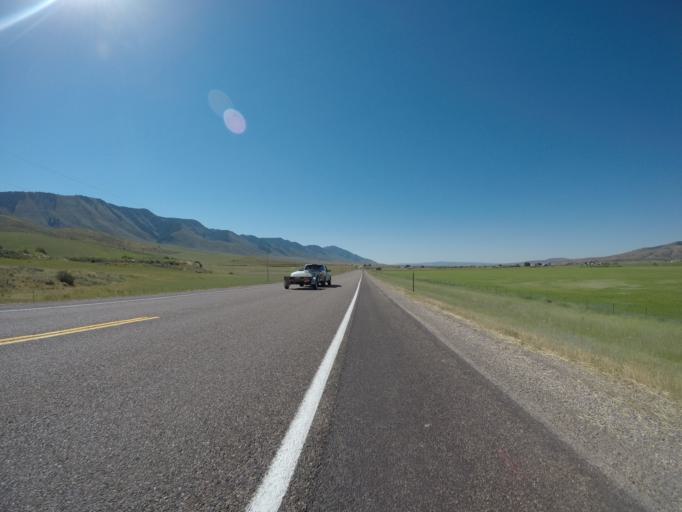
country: US
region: Idaho
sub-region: Bear Lake County
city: Montpelier
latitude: 42.3676
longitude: -111.0523
